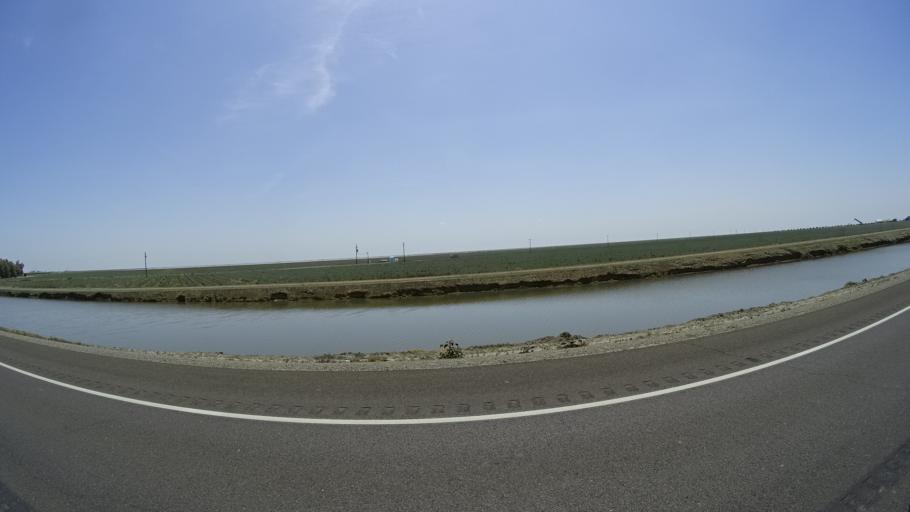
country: US
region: California
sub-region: Kings County
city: Stratford
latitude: 36.1350
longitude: -119.8803
